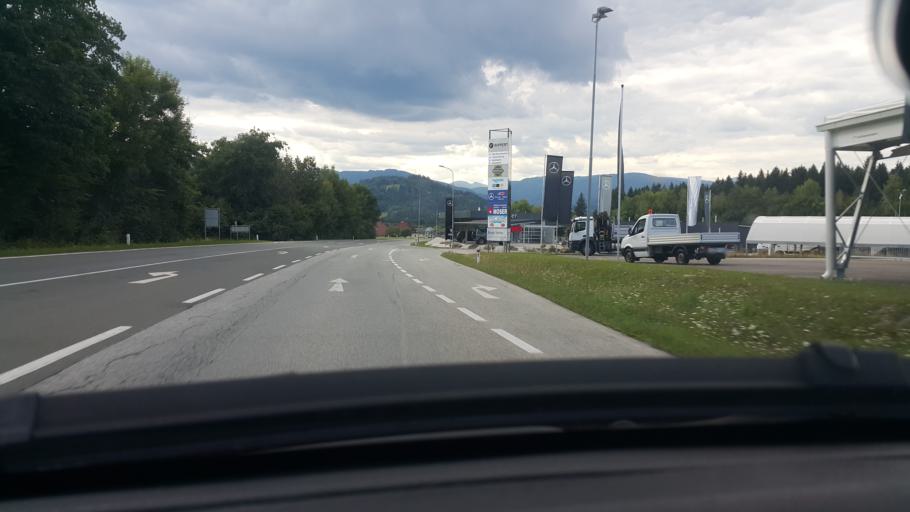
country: AT
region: Carinthia
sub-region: Politischer Bezirk Feldkirchen
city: Feldkirchen in Karnten
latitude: 46.6928
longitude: 14.1276
